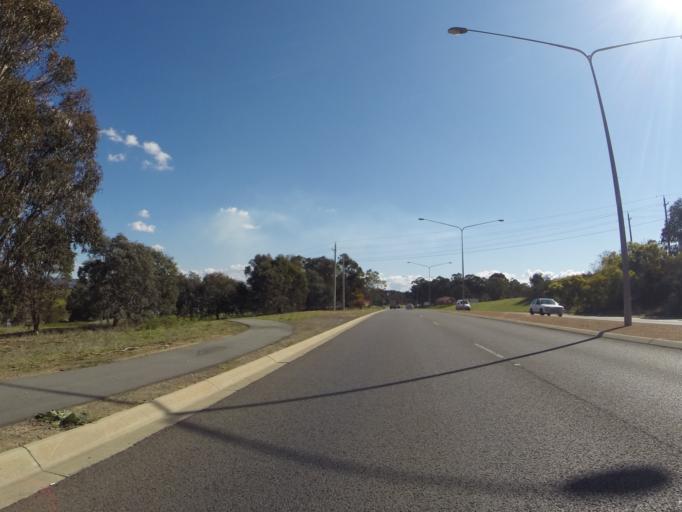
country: AU
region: Australian Capital Territory
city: Forrest
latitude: -35.3018
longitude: 149.1566
